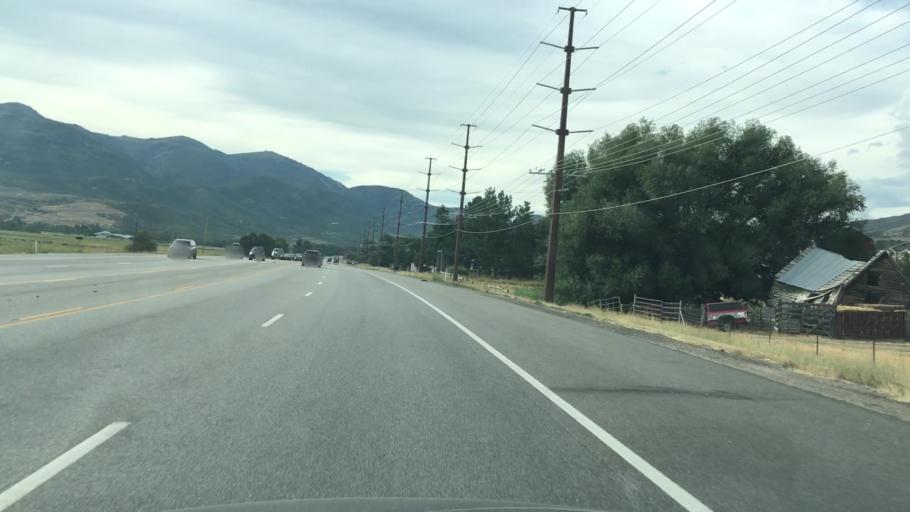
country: US
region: Utah
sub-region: Wasatch County
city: Heber
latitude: 40.5360
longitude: -111.4102
